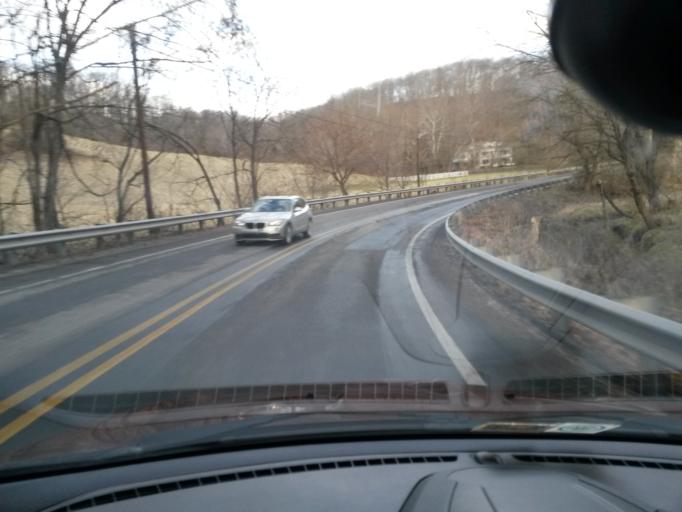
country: US
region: West Virginia
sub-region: Monroe County
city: Union
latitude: 37.5728
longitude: -80.5693
